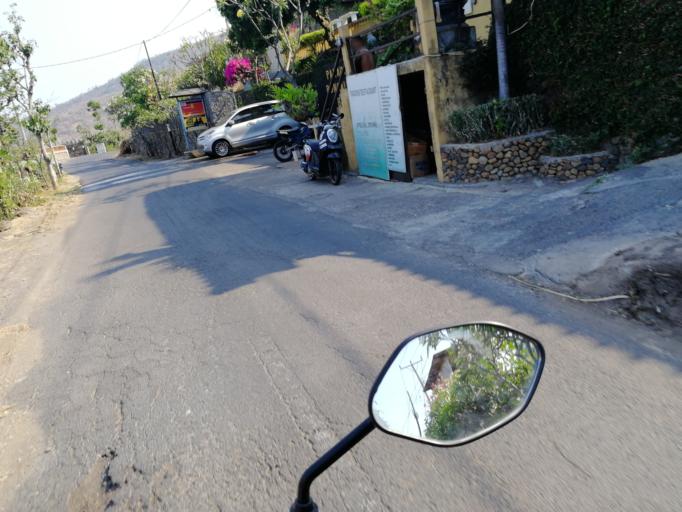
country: ID
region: Bali
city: Biaslantang Kaler
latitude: -8.3602
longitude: 115.6981
